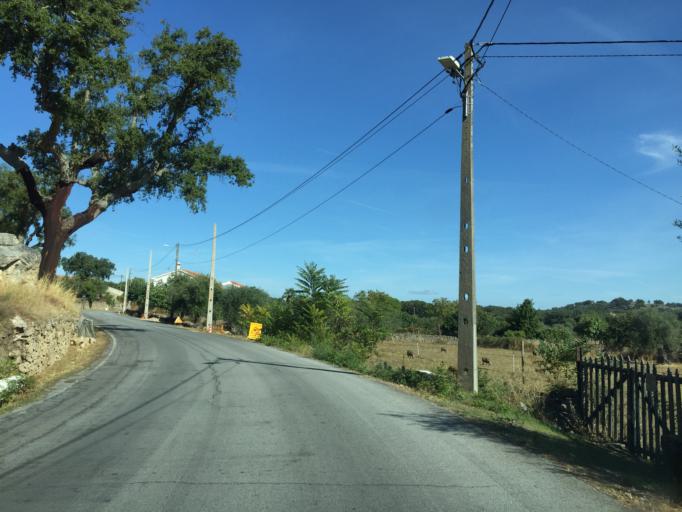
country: PT
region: Portalegre
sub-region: Marvao
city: Marvao
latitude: 39.4204
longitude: -7.3519
